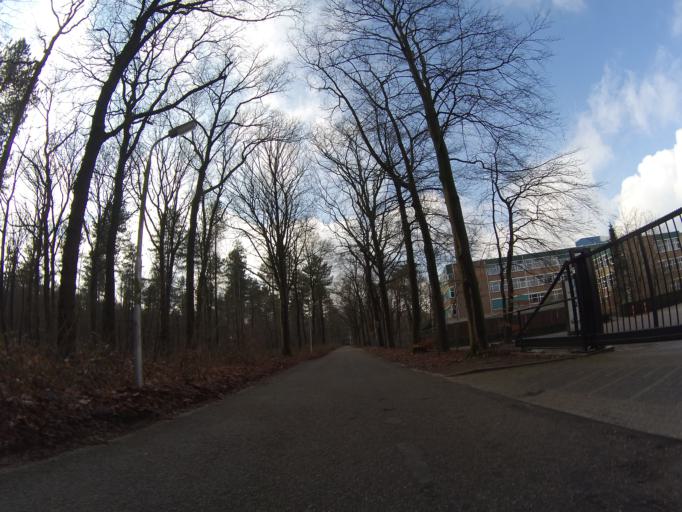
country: NL
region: Utrecht
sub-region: Gemeente Amersfoort
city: Amersfoort
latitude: 52.1365
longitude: 5.3526
